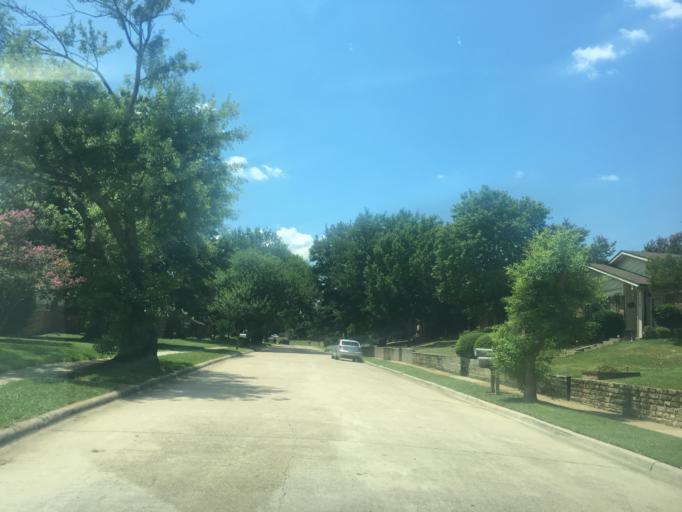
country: US
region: Texas
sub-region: Denton County
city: Lewisville
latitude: 33.0234
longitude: -97.0045
